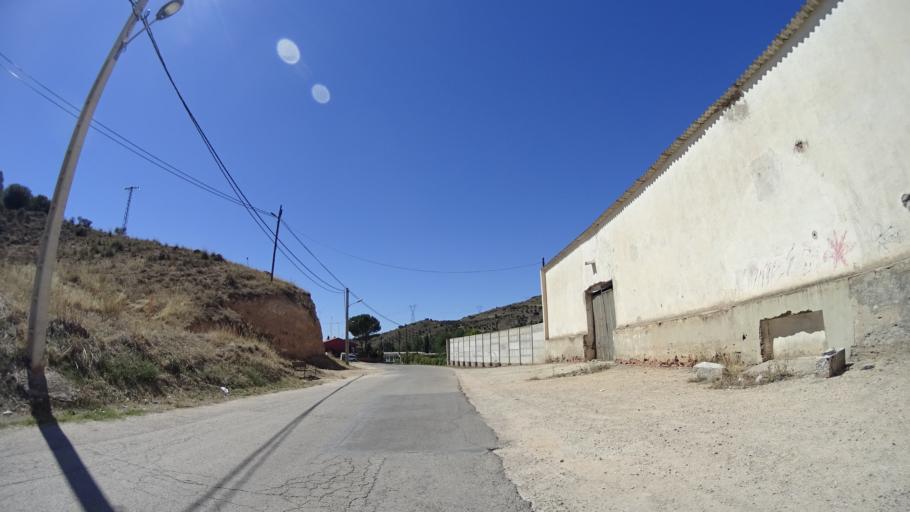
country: ES
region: Madrid
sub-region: Provincia de Madrid
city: Perales de Tajuna
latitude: 40.2292
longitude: -3.3529
